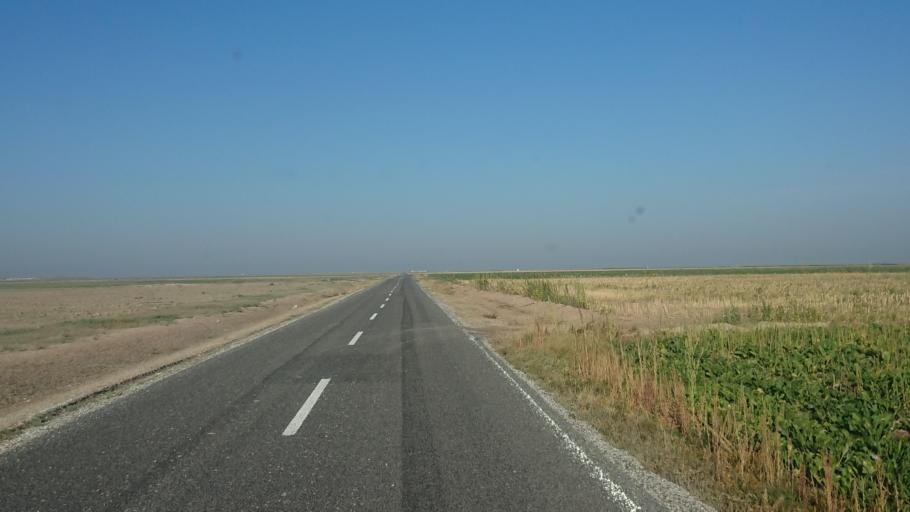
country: TR
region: Aksaray
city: Yesilova
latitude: 38.3876
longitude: 33.7922
